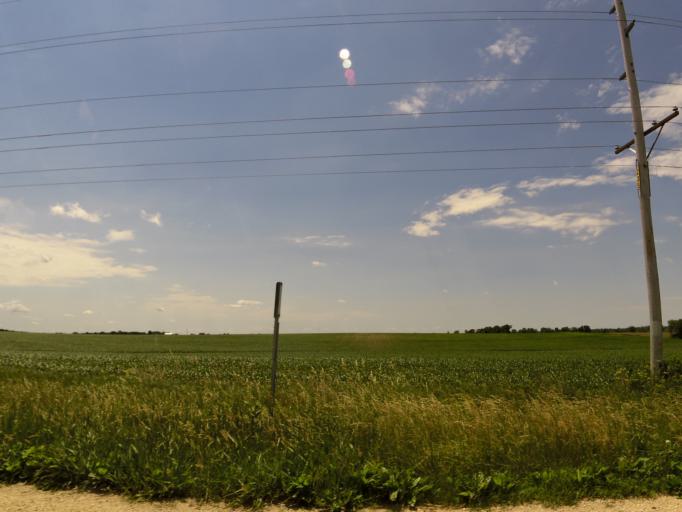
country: US
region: Iowa
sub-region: Buchanan County
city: Fairbank
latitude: 42.7147
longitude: -92.1488
